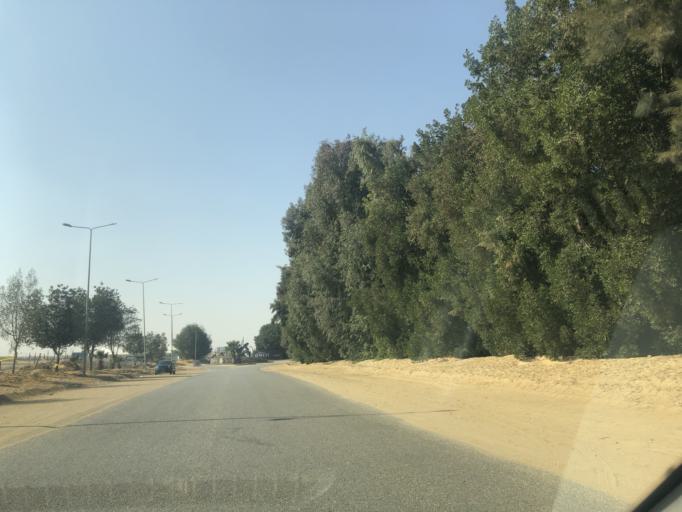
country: EG
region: Al Jizah
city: Madinat Sittah Uktubar
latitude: 29.9617
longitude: 31.0034
